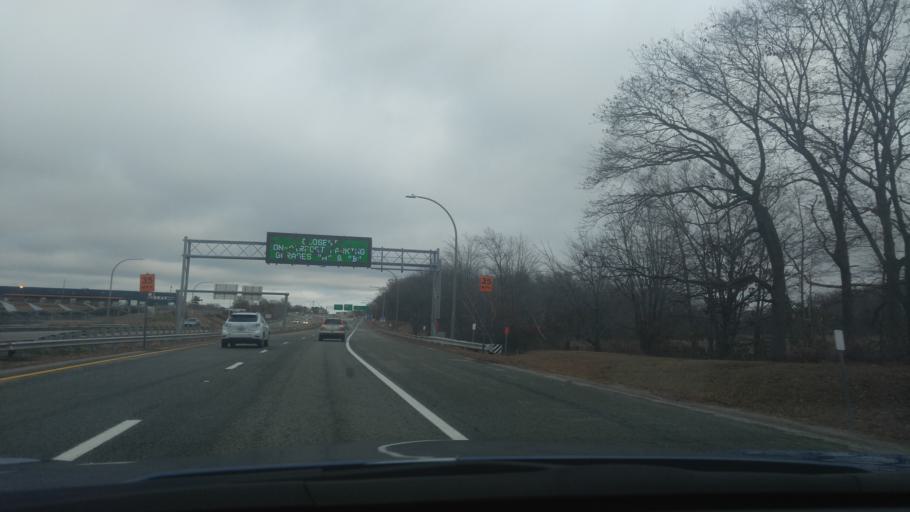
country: US
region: Rhode Island
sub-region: Kent County
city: Warwick
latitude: 41.7258
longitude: -71.4522
